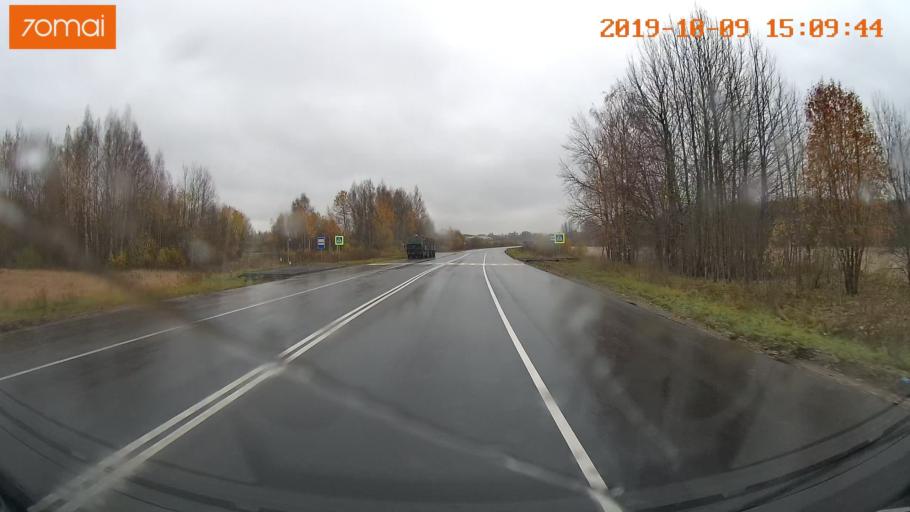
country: RU
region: Kostroma
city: Susanino
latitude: 58.1874
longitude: 41.6488
